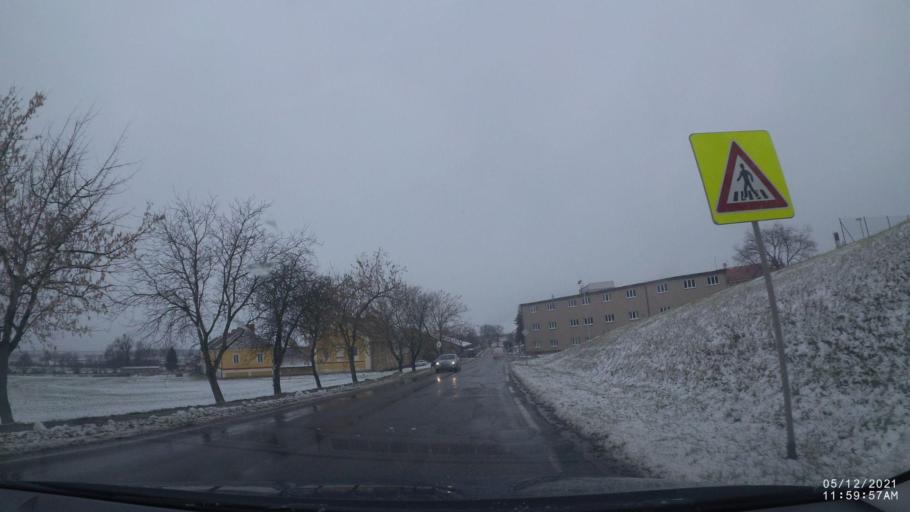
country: CZ
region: Kralovehradecky
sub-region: Okres Rychnov nad Kneznou
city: Opocno
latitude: 50.2751
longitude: 16.0943
